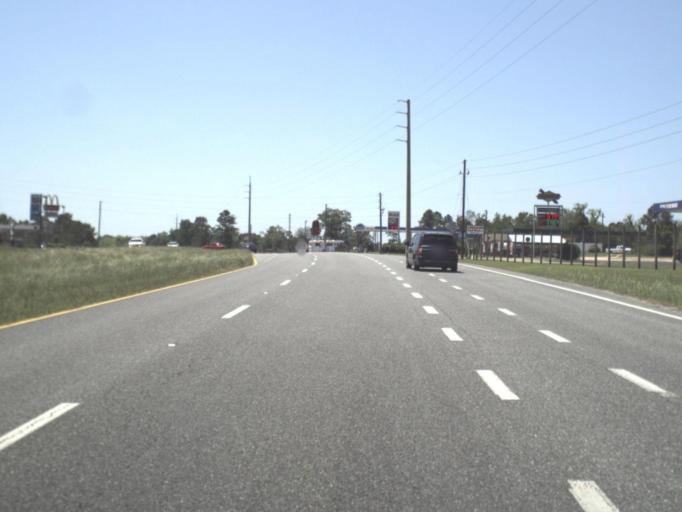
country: US
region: Florida
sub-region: Jefferson County
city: Monticello
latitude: 30.4739
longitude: -83.8907
